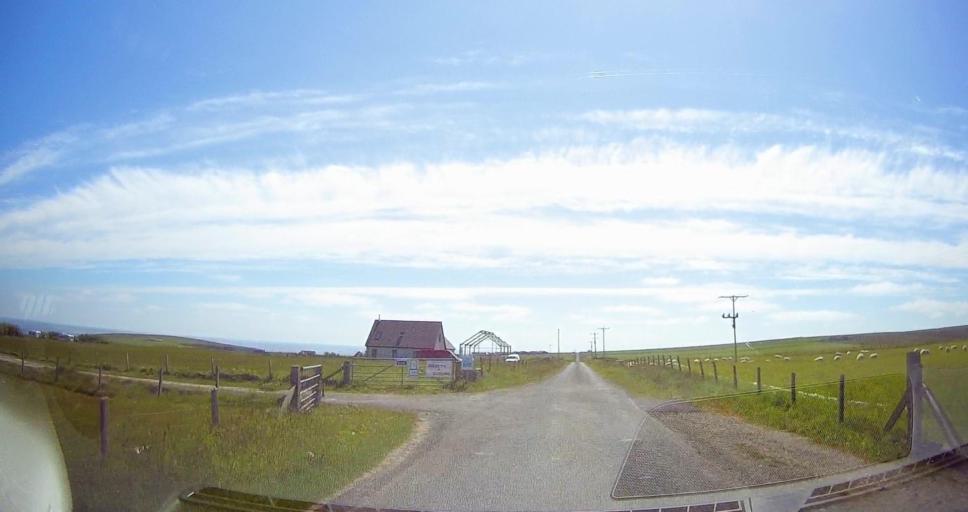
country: GB
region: Scotland
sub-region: Orkney Islands
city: Kirkwall
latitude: 58.8277
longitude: -2.9122
